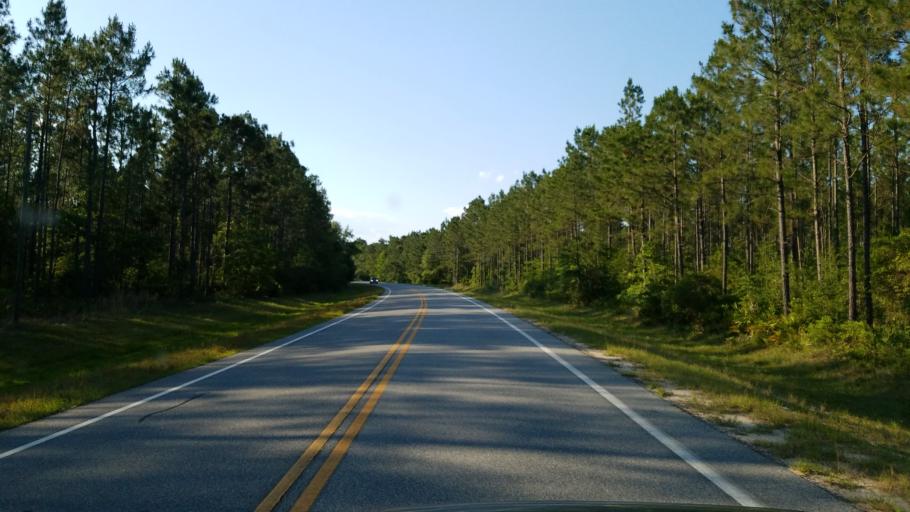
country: US
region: Georgia
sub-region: Lanier County
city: Lakeland
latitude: 30.8850
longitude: -83.0532
